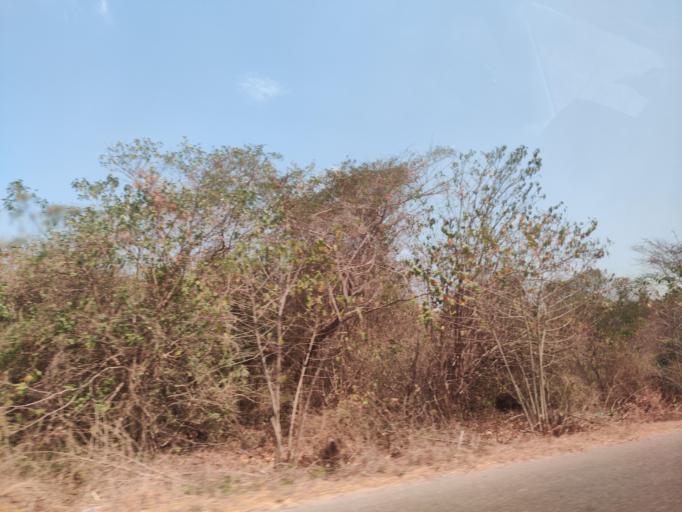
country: CO
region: Bolivar
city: Turbana
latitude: 10.2761
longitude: -75.5306
